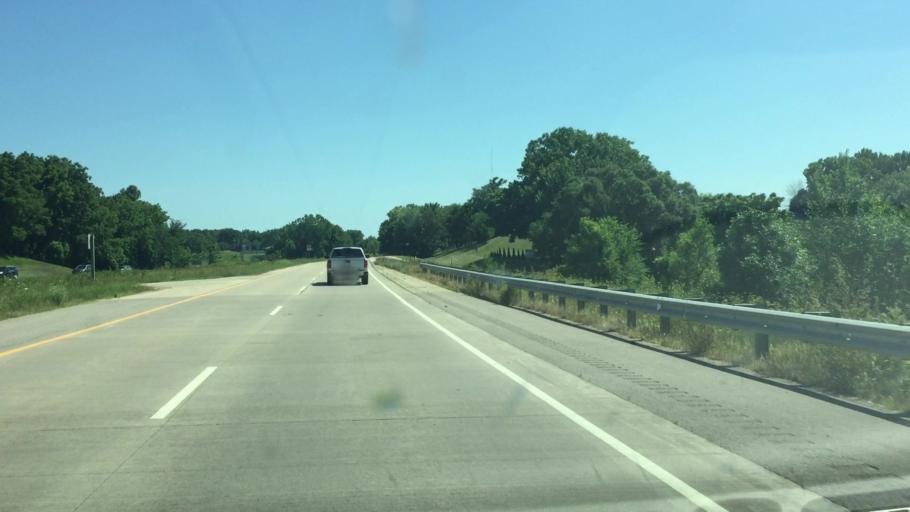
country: US
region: Illinois
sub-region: Jo Daviess County
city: East Dubuque
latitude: 42.5529
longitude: -90.6098
